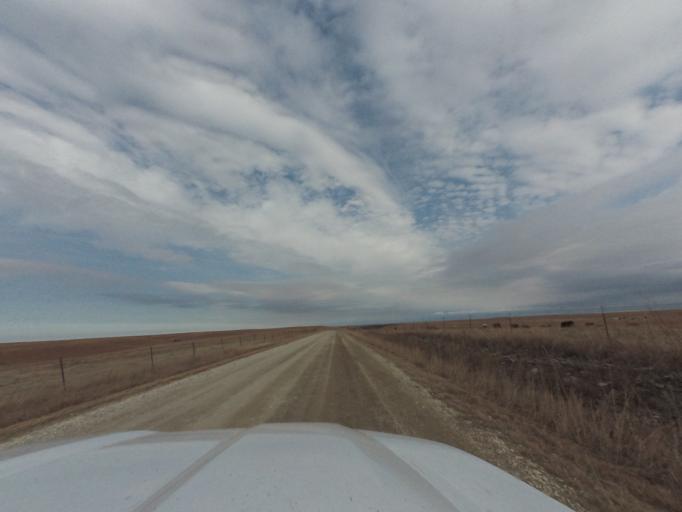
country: US
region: Kansas
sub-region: Chase County
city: Cottonwood Falls
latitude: 38.2442
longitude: -96.7305
